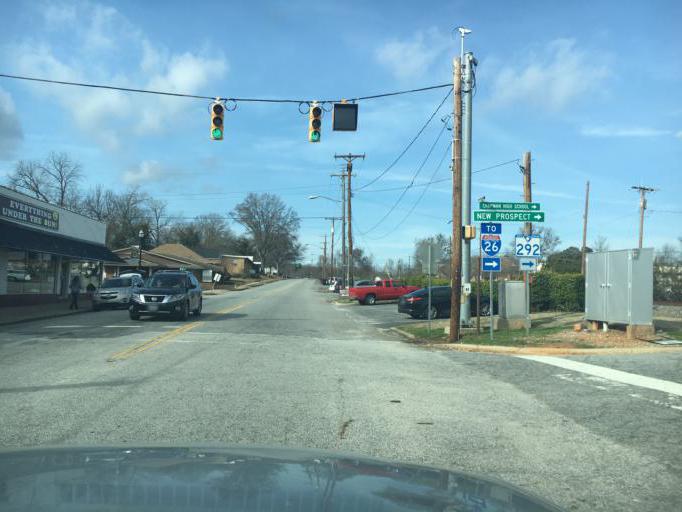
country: US
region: South Carolina
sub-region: Spartanburg County
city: Inman
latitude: 35.0486
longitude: -82.0908
